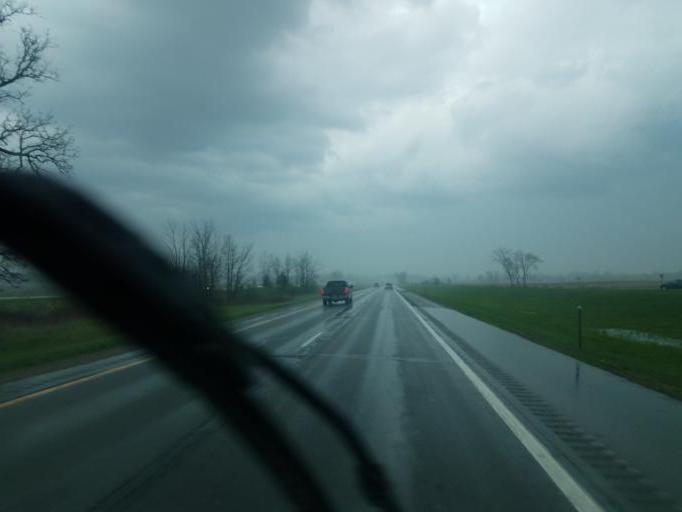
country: US
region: Michigan
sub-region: Ingham County
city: Webberville
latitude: 42.6505
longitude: -84.1286
